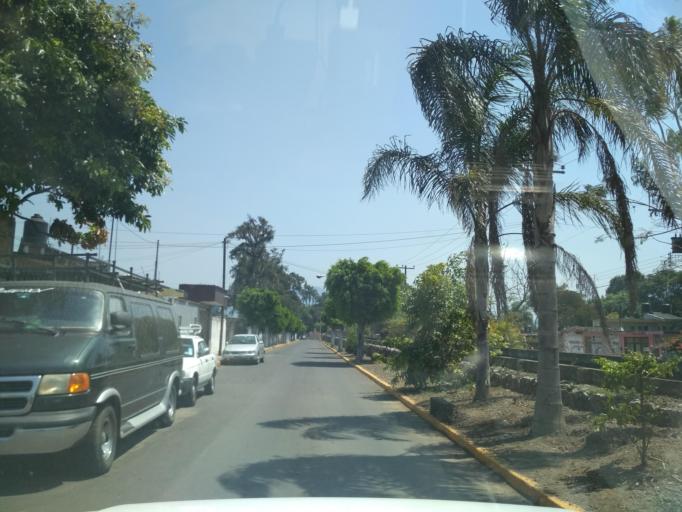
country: MX
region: Veracruz
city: Rio Blanco
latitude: 18.8362
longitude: -97.1108
